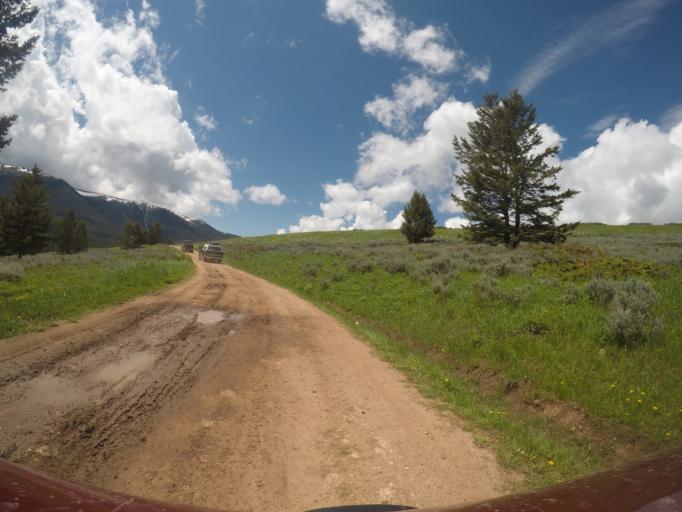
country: US
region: Wyoming
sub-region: Big Horn County
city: Lovell
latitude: 45.1759
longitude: -108.4345
